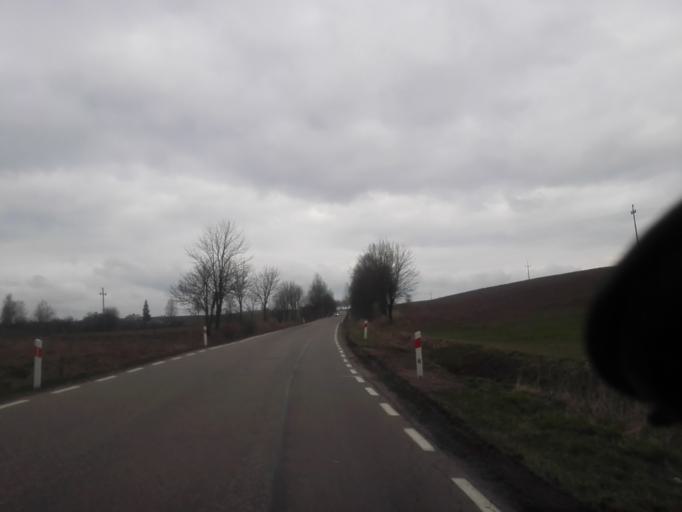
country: PL
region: Podlasie
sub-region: Suwalki
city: Suwalki
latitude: 54.2332
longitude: 22.9130
